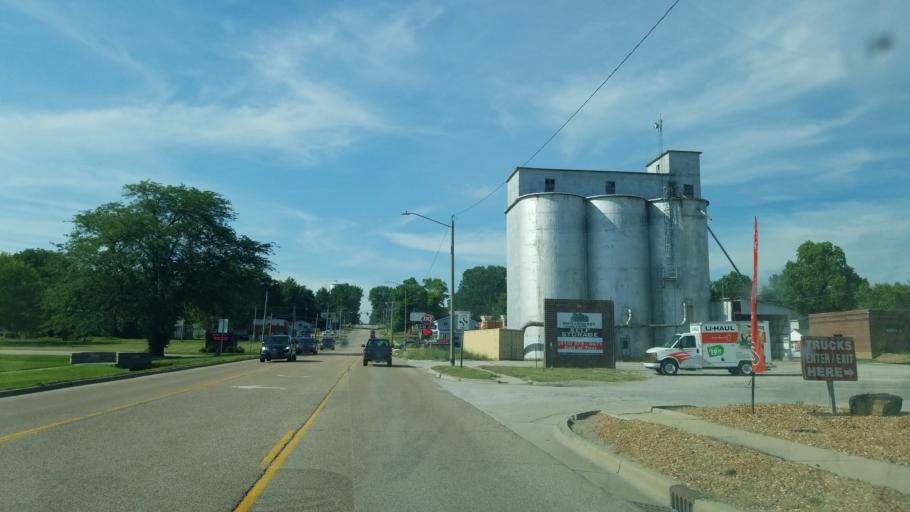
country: US
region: Illinois
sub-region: Saint Clair County
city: Lebanon
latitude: 38.5994
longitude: -89.8076
